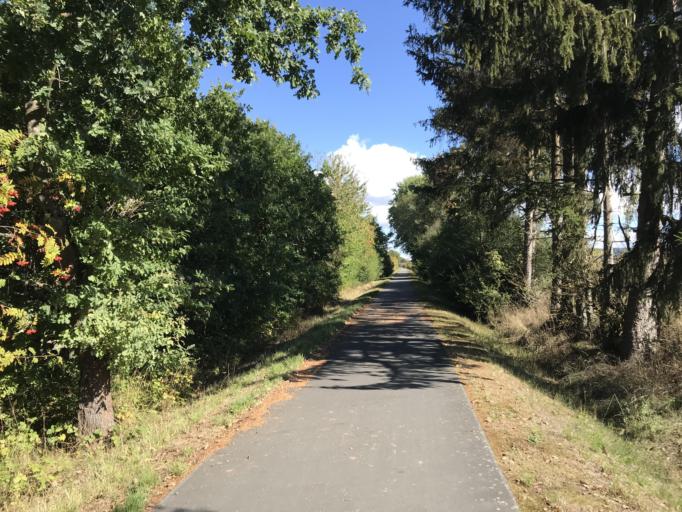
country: DE
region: Hesse
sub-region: Regierungsbezirk Kassel
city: Sachsenhausen
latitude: 51.2664
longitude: 8.9651
